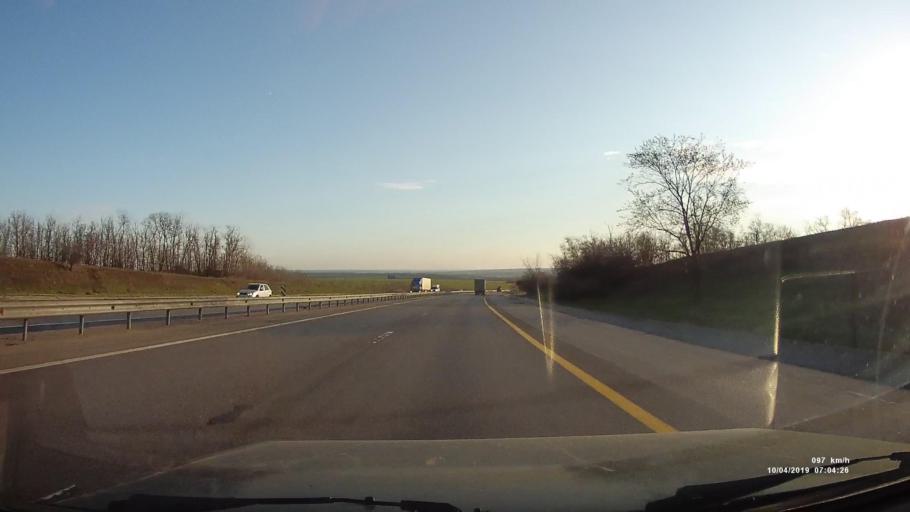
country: RU
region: Rostov
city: Mayskiy
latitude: 47.6370
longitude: 40.0003
